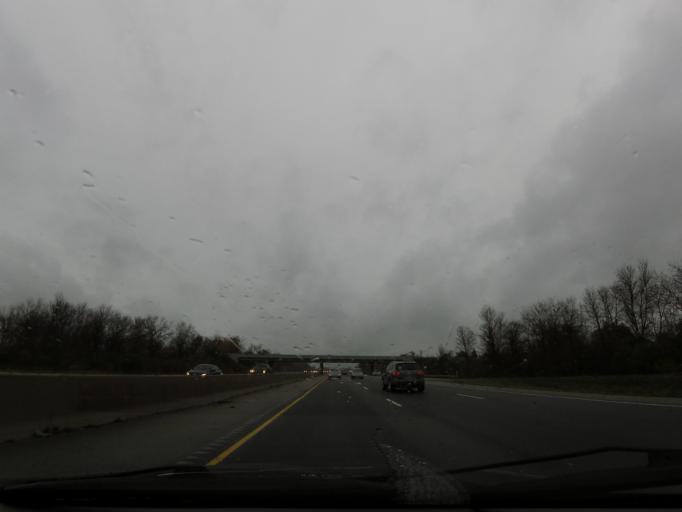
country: CA
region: Ontario
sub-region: Wellington County
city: Guelph
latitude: 43.4474
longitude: -80.1788
